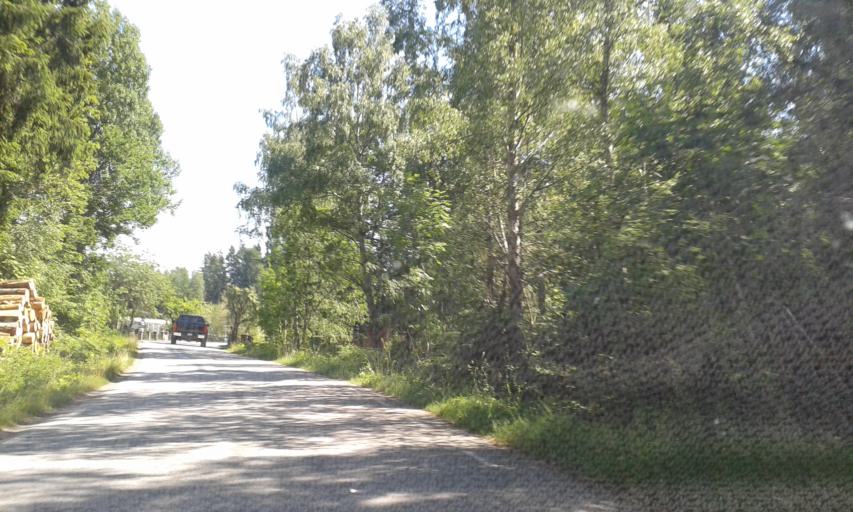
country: SE
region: Blekinge
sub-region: Karlskrona Kommun
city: Rodeby
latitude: 56.2427
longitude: 15.5609
